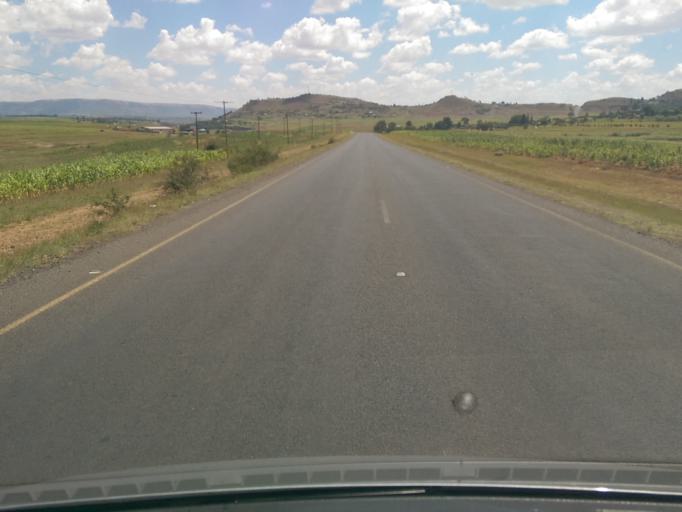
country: LS
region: Maseru
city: Maseru
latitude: -29.4200
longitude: 27.6554
